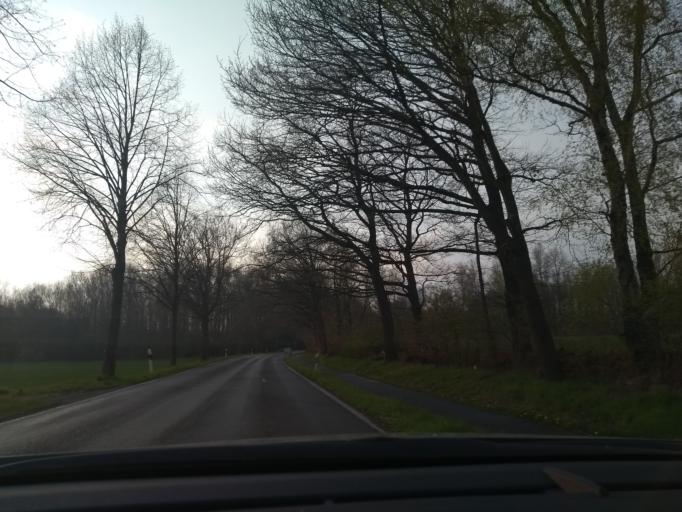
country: DE
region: North Rhine-Westphalia
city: Selm
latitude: 51.6419
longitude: 7.4680
